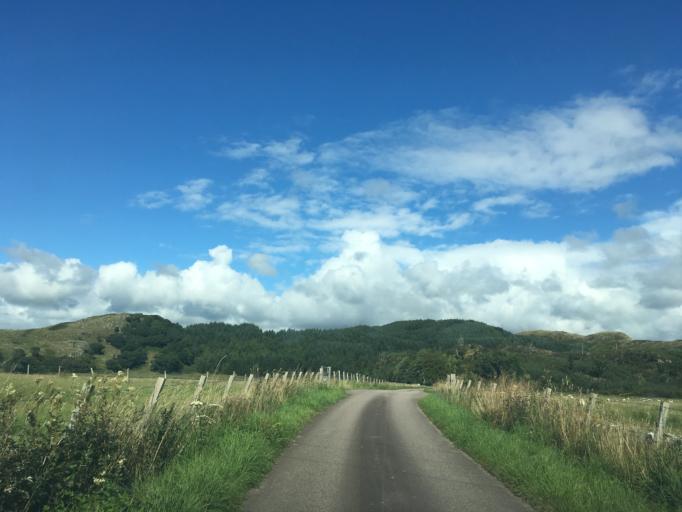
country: GB
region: Scotland
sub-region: Argyll and Bute
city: Lochgilphead
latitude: 56.0864
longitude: -5.4737
